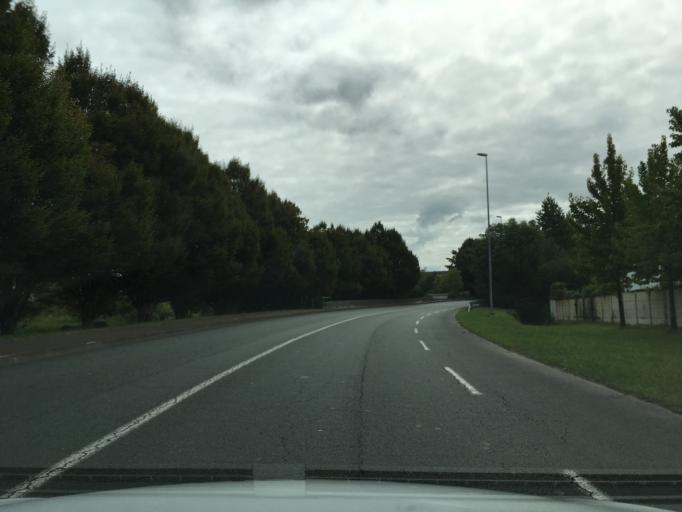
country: FR
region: Aquitaine
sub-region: Departement des Pyrenees-Atlantiques
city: Bayonne
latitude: 43.4811
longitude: -1.4585
